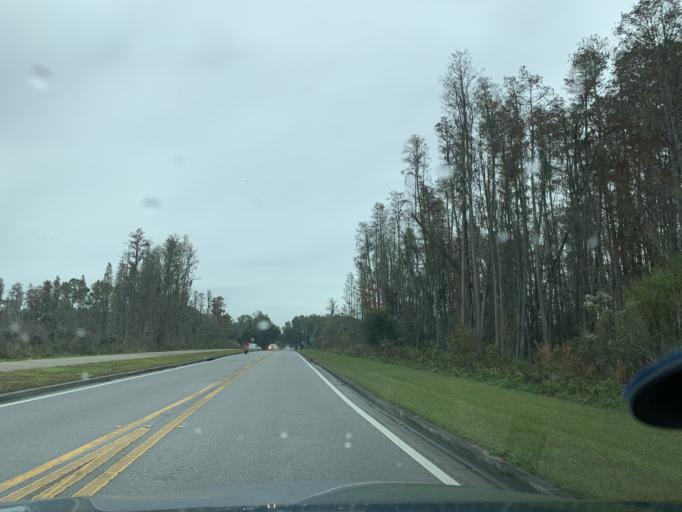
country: US
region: Florida
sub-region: Pasco County
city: Wesley Chapel
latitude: 28.2422
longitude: -82.3203
